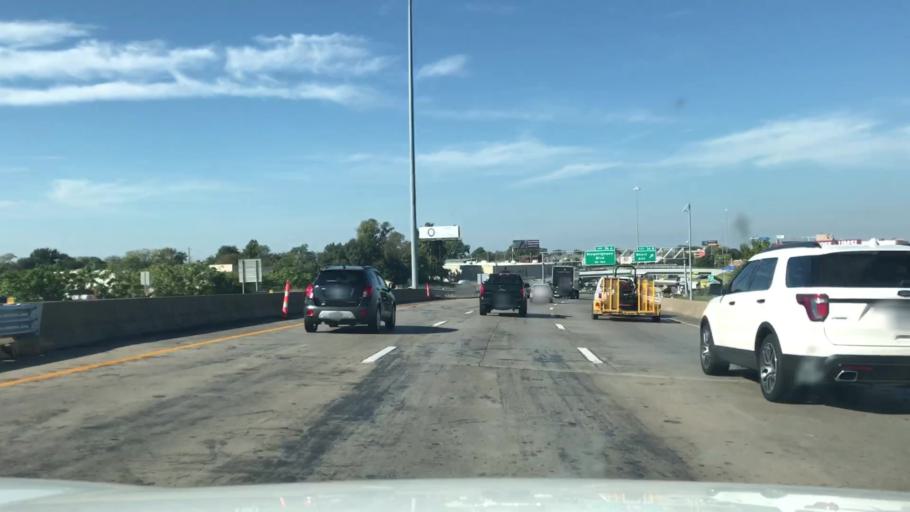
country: US
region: Missouri
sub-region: City of Saint Louis
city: St. Louis
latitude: 38.6314
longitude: -90.2488
